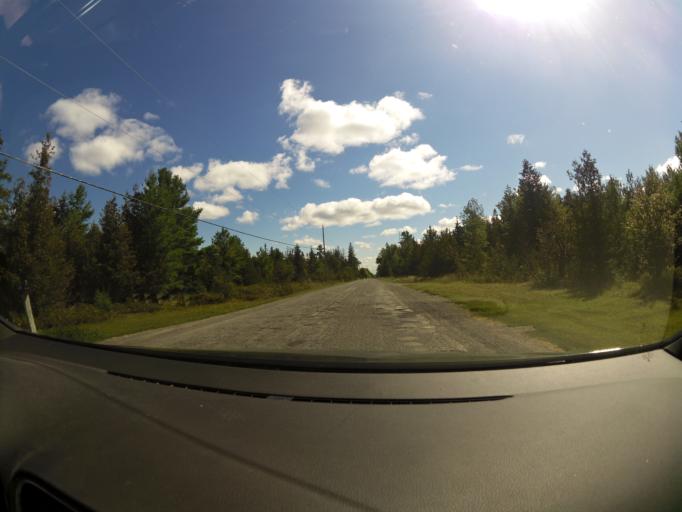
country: CA
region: Ontario
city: Carleton Place
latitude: 45.2483
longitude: -76.1687
